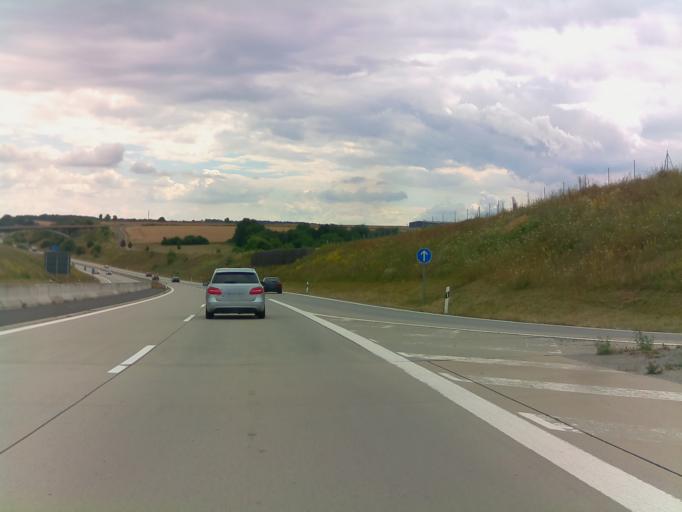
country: DE
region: Bavaria
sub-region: Regierungsbezirk Unterfranken
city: Rodelmaier
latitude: 50.3290
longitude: 10.2909
